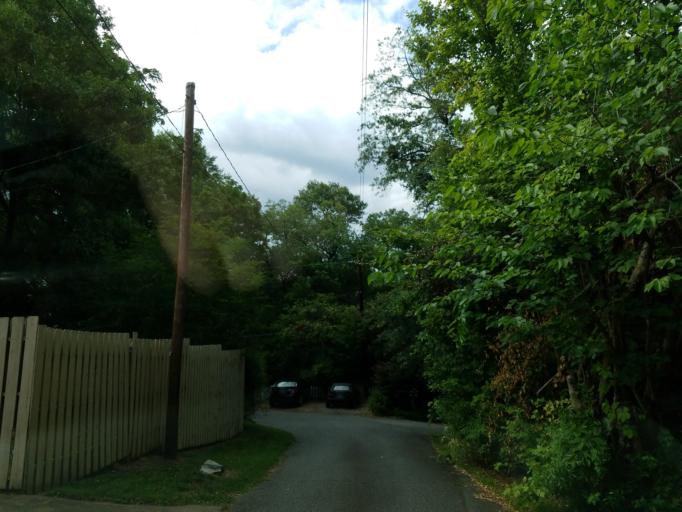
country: US
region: Georgia
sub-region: Fulton County
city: Roswell
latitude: 34.0146
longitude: -84.3575
